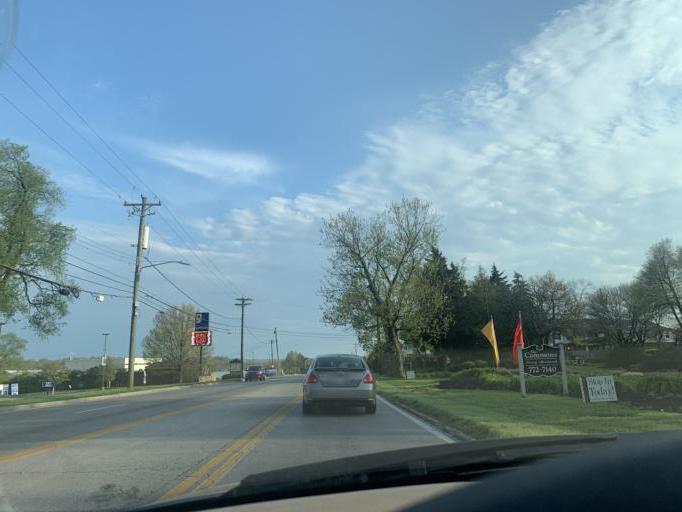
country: US
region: Ohio
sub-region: Hamilton County
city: Glendale
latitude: 39.2642
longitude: -84.4693
